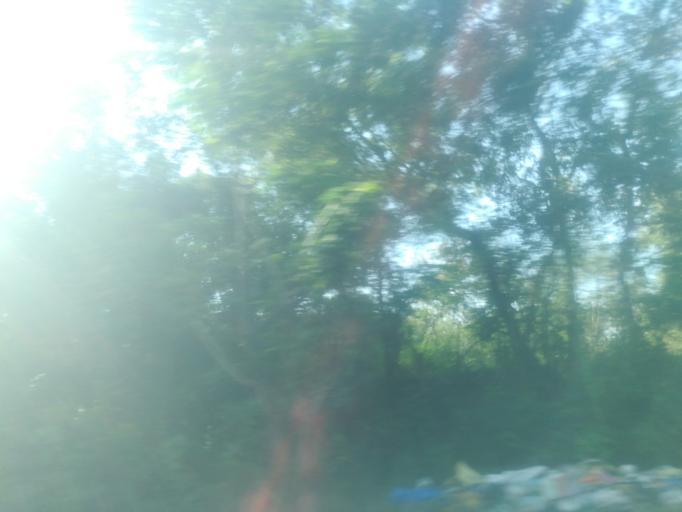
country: NG
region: Ogun
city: Abeokuta
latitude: 7.1567
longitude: 3.2635
